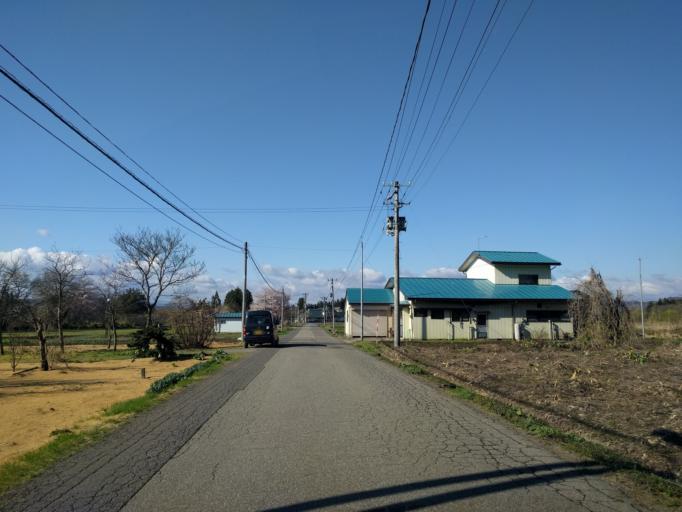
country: JP
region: Fukushima
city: Kitakata
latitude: 37.6444
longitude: 139.7916
